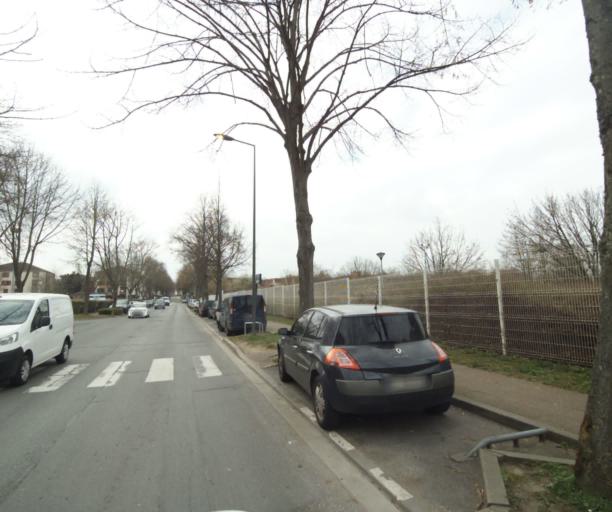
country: FR
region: Ile-de-France
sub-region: Departement du Val-d'Oise
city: Vaureal
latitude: 49.0508
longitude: 2.0336
